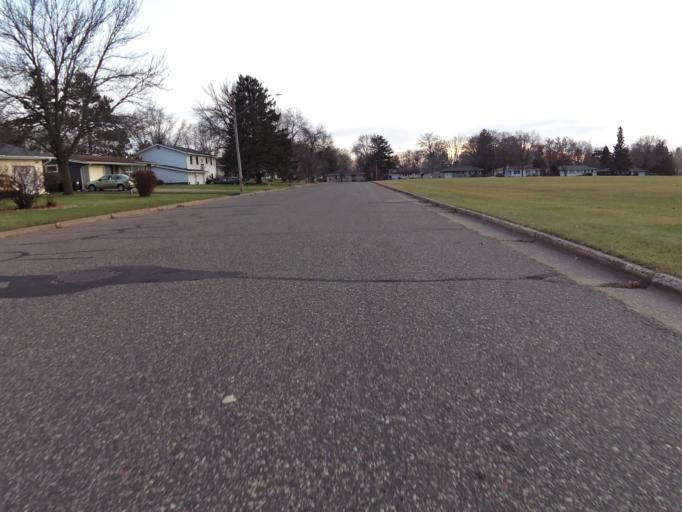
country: US
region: Wisconsin
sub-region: Saint Croix County
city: Hudson
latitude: 44.9676
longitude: -92.7369
